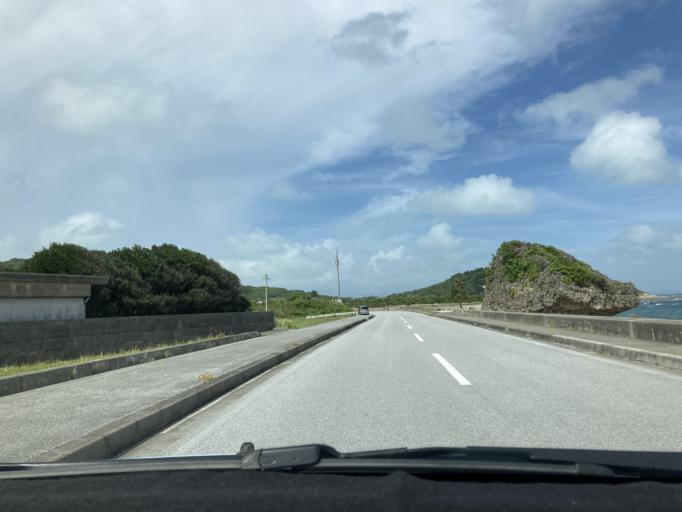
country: JP
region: Okinawa
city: Ginowan
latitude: 26.1806
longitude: 127.8222
